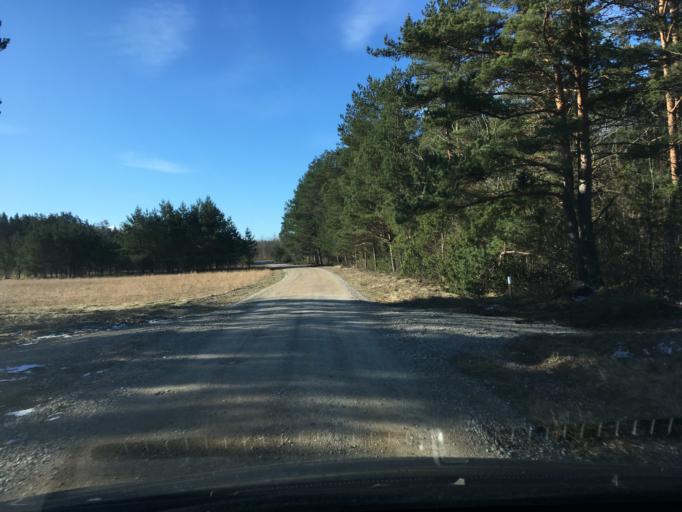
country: EE
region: Laeaene
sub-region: Lihula vald
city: Lihula
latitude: 58.5750
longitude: 23.6987
